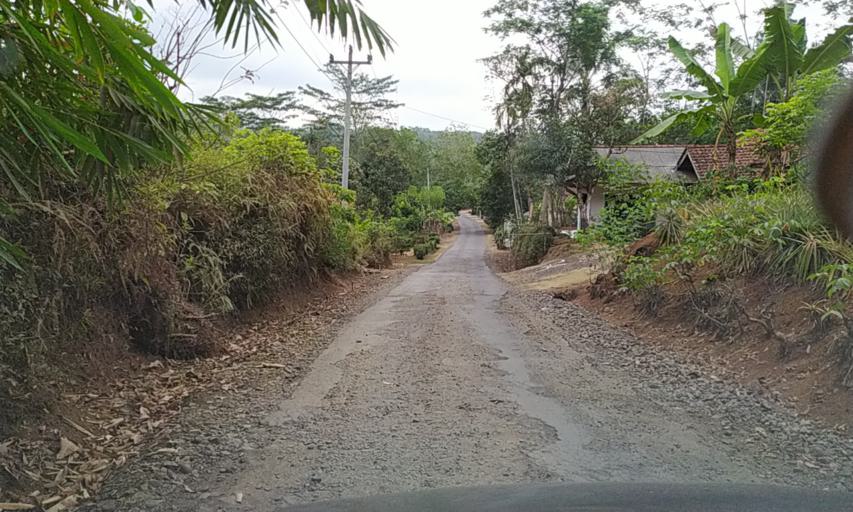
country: ID
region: Central Java
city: Ciwalen
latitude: -7.2878
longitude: 108.6102
